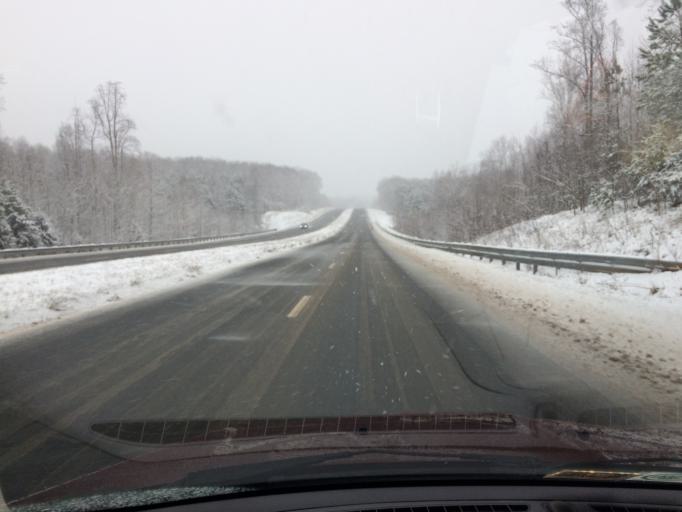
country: US
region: Virginia
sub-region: Amherst County
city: Madison Heights
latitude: 37.4673
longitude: -79.1081
